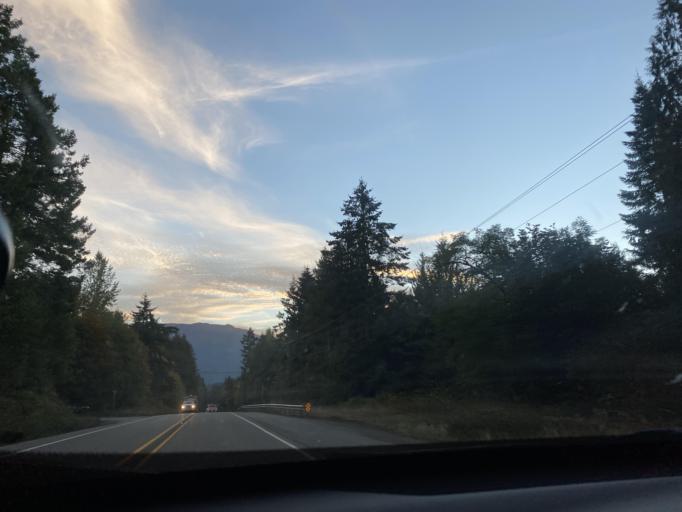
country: US
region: Washington
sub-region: Clallam County
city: Port Angeles
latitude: 48.0941
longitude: -123.5475
